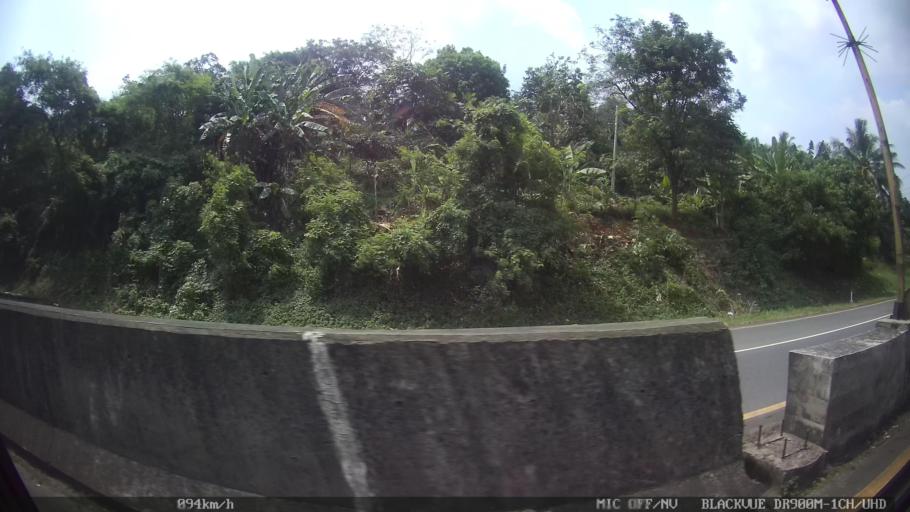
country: ID
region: Banten
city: Curug
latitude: -5.9830
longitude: 106.0245
